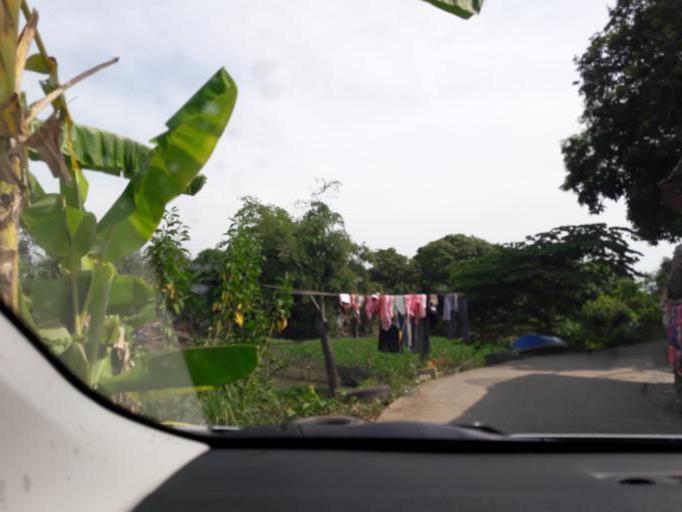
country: TH
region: Ang Thong
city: Ang Thong
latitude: 14.5799
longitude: 100.4418
